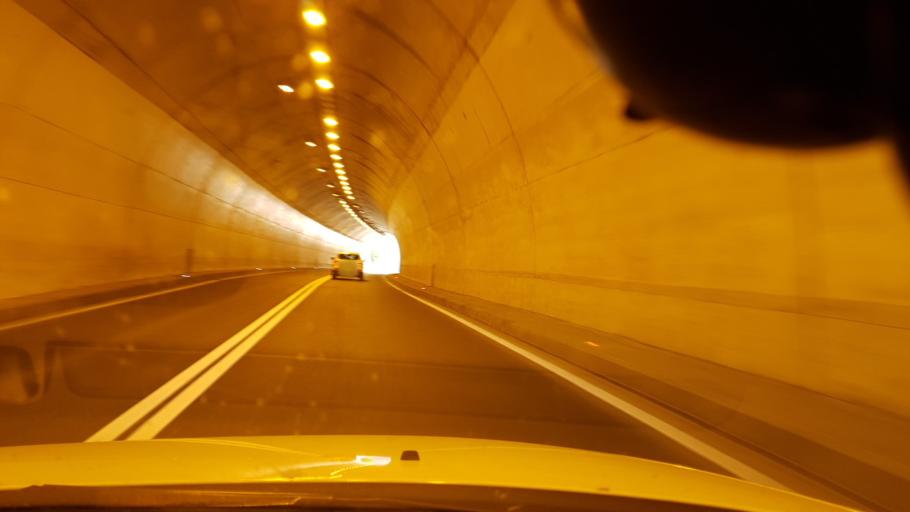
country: SI
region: Zetale
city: Zetale
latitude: 46.2484
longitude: 15.8505
